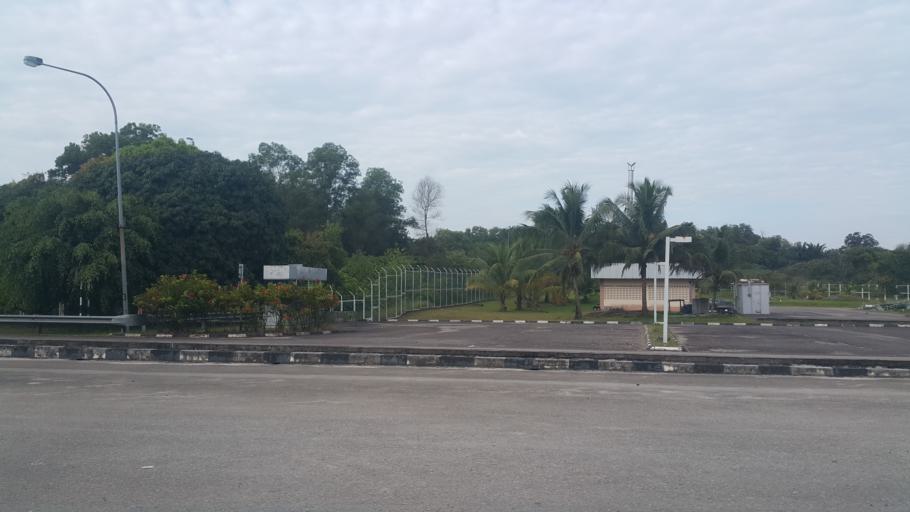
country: MY
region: Johor
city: Pekan Nenas
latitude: 1.3780
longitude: 103.5964
